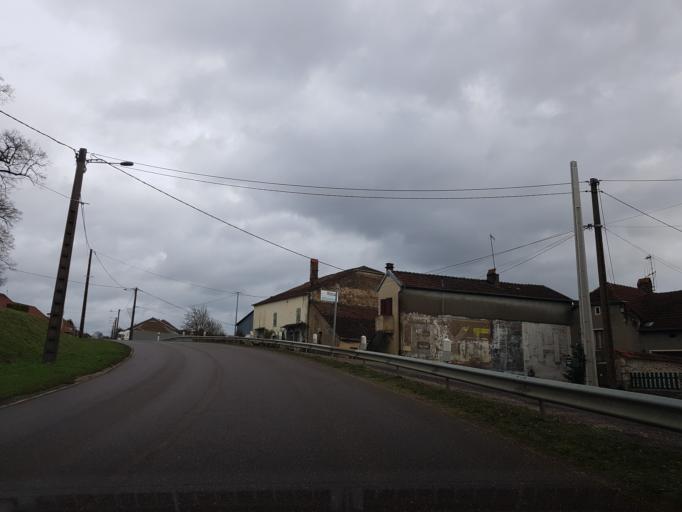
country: FR
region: Franche-Comte
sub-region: Departement de la Haute-Saone
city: Jussey
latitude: 47.7209
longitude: 5.8414
